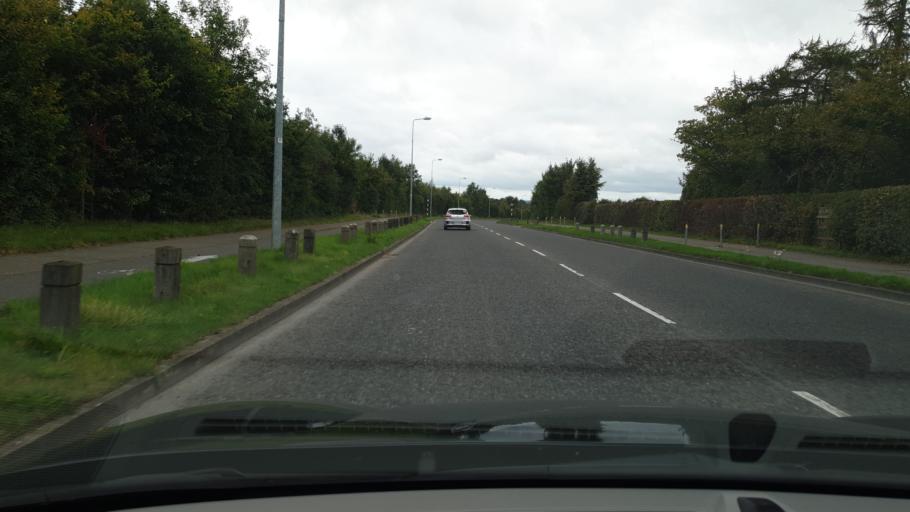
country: IE
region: Leinster
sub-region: Kildare
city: Naas
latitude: 53.2192
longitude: -6.6872
